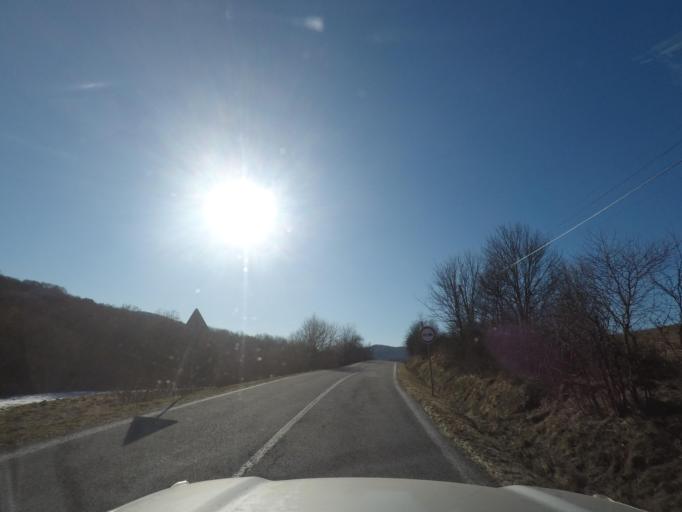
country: SK
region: Presovsky
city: Snina
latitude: 49.1272
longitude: 22.1113
